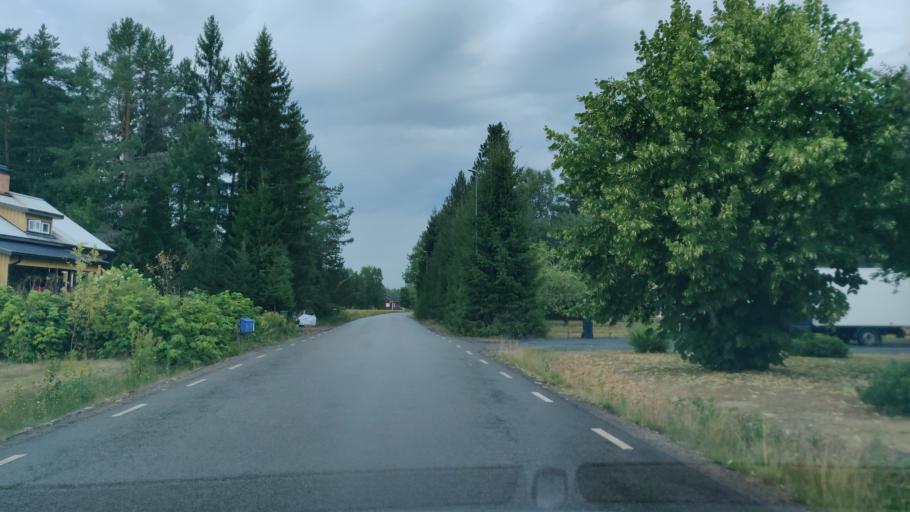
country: SE
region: Vaermland
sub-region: Munkfors Kommun
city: Munkfors
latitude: 59.8614
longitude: 13.5493
